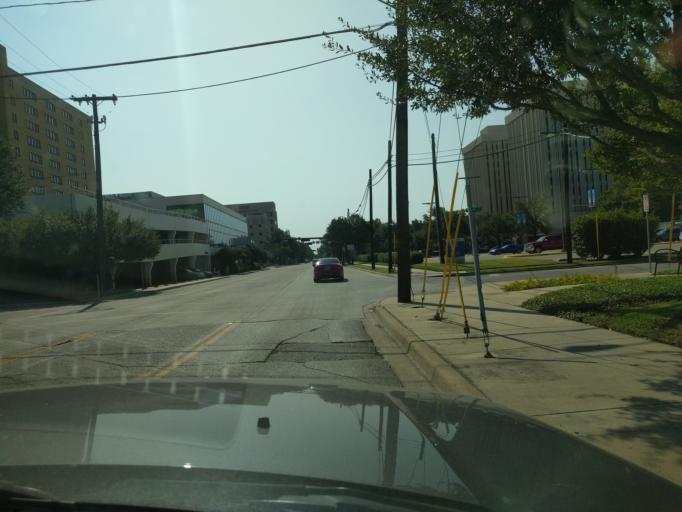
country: US
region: Texas
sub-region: Dallas County
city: Dallas
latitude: 32.7928
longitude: -96.7802
